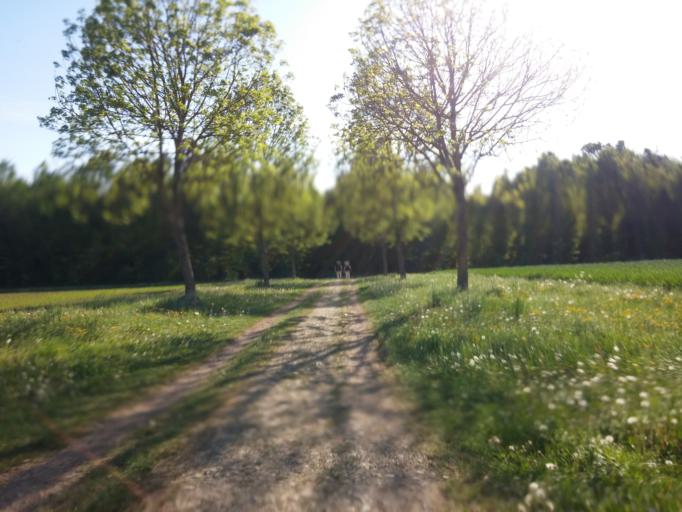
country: DE
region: Bavaria
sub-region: Upper Bavaria
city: Vaterstetten
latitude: 48.1110
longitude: 11.7646
